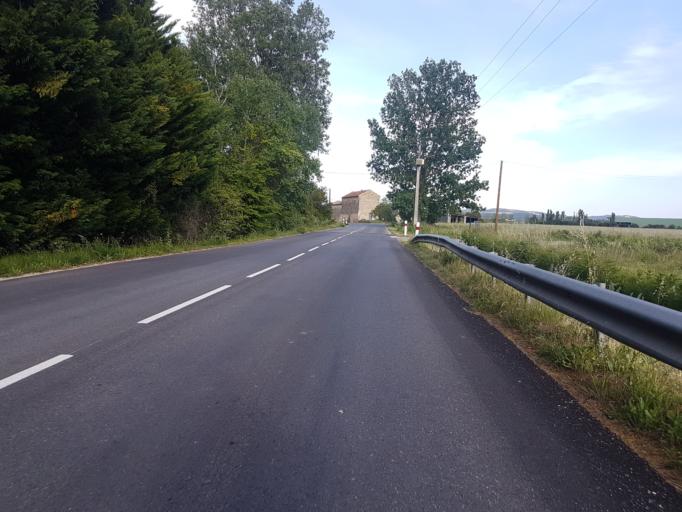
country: FR
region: Languedoc-Roussillon
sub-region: Departement du Gard
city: Pont-Saint-Esprit
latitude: 44.2584
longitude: 4.6681
